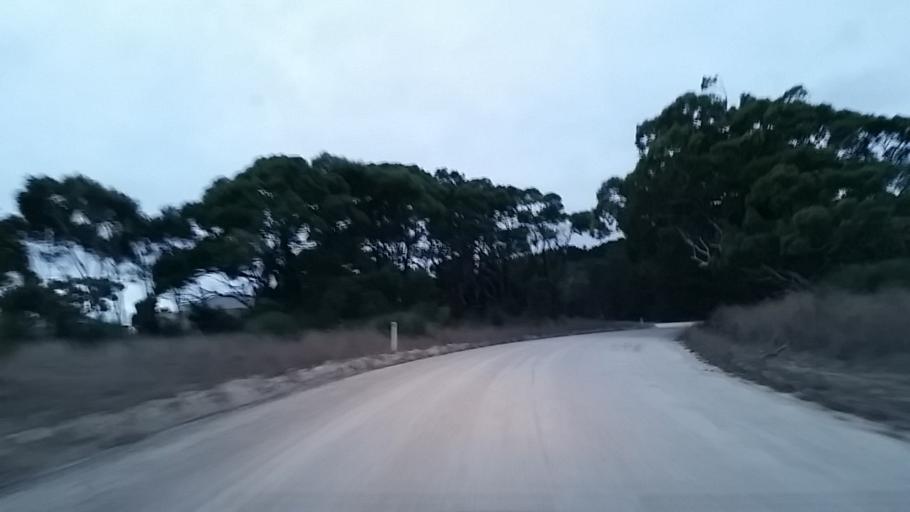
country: AU
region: South Australia
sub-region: Yankalilla
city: Normanville
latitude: -35.6098
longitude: 138.1752
